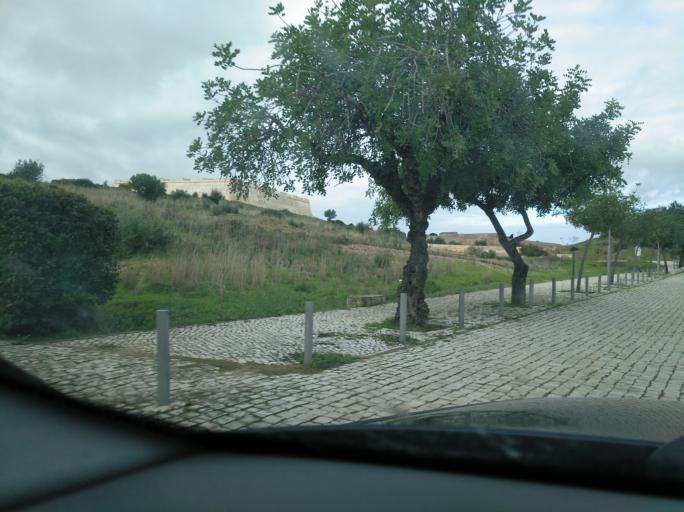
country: PT
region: Faro
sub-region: Castro Marim
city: Castro Marim
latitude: 37.2147
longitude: -7.4407
